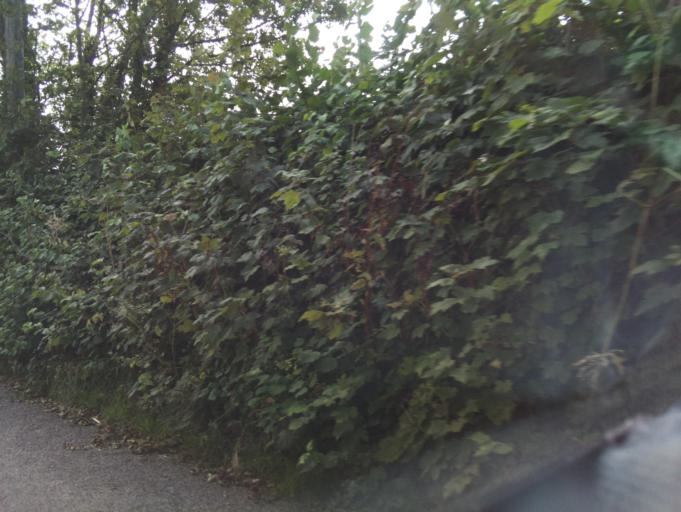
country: GB
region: England
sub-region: Borough of Torbay
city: Paignton
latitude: 50.4006
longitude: -3.6052
